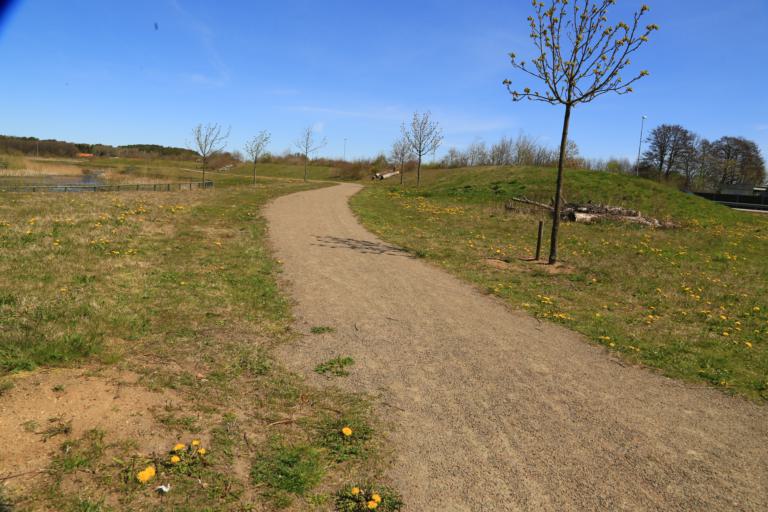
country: SE
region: Halland
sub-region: Varbergs Kommun
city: Traslovslage
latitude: 57.0841
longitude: 12.2825
